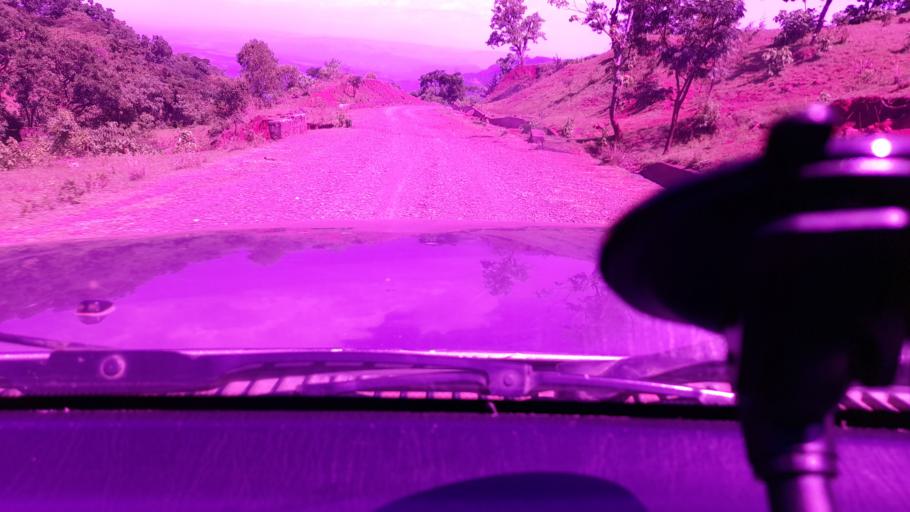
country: ET
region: Oromiya
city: Jima
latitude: 7.8316
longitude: 37.5465
